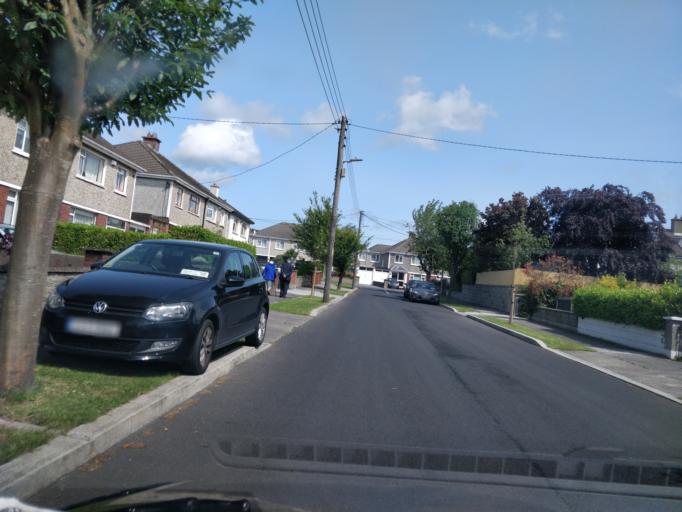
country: IE
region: Leinster
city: Dundrum
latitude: 53.2851
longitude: -6.2543
